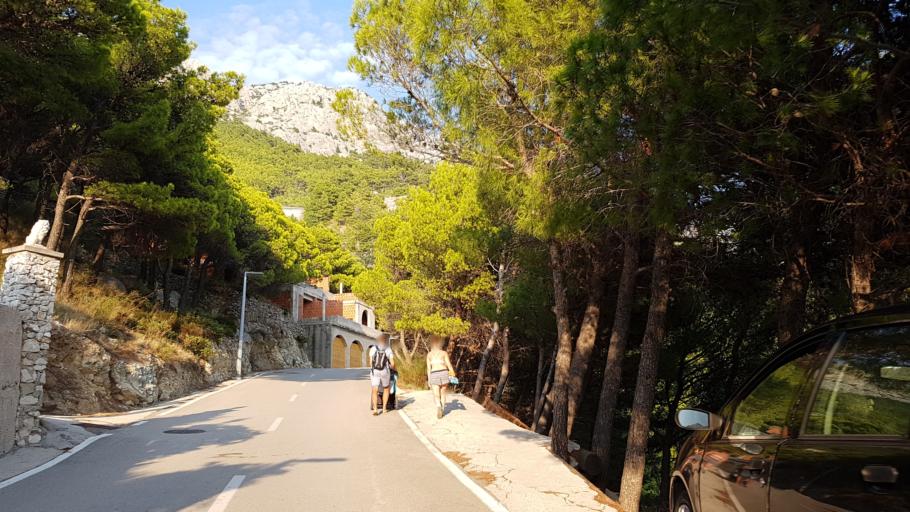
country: HR
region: Splitsko-Dalmatinska
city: Donja Brela
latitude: 43.3872
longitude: 16.9015
